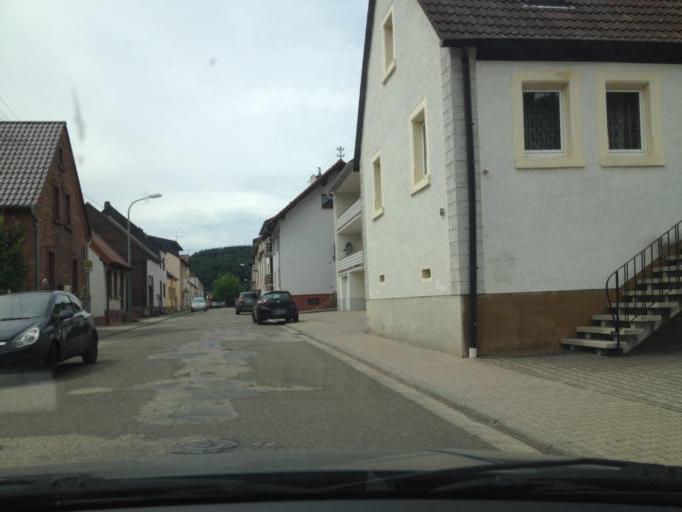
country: DE
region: Rheinland-Pfalz
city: Linden
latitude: 49.3489
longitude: 7.6510
